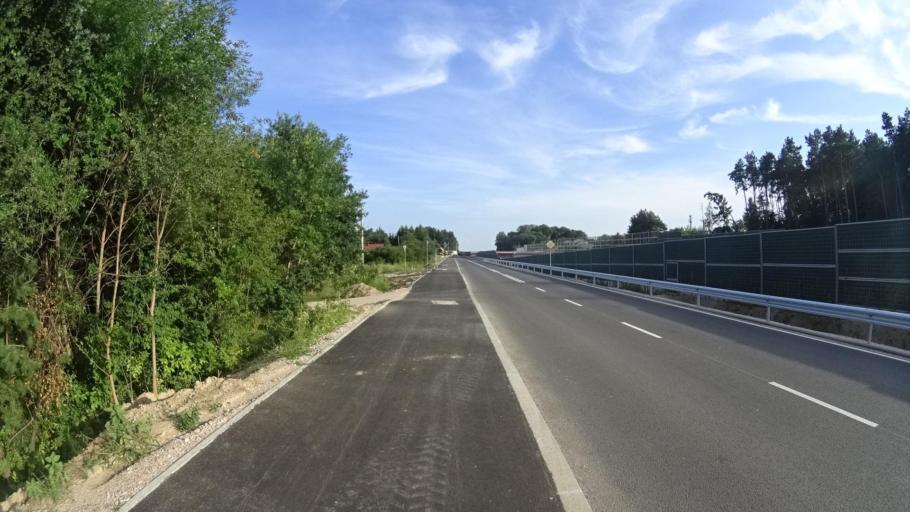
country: PL
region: Masovian Voivodeship
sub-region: Powiat grojecki
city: Grojec
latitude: 51.9111
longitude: 20.8565
